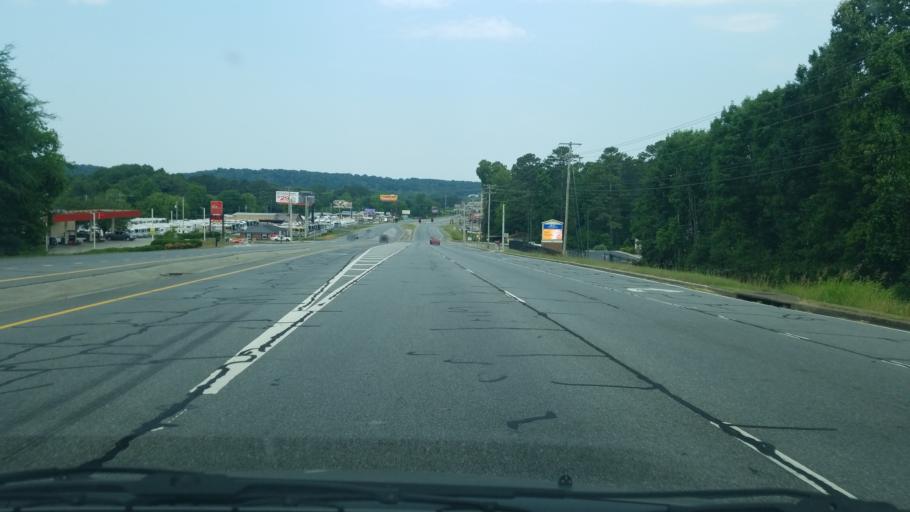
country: US
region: Georgia
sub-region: Catoosa County
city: Indian Springs
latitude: 34.9299
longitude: -85.1698
